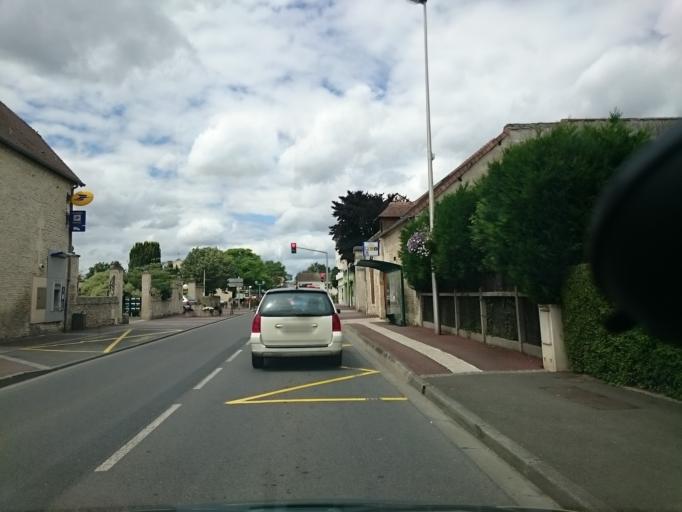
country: FR
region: Lower Normandy
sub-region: Departement du Calvados
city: Cormelles-le-Royal
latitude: 49.1542
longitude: -0.3297
